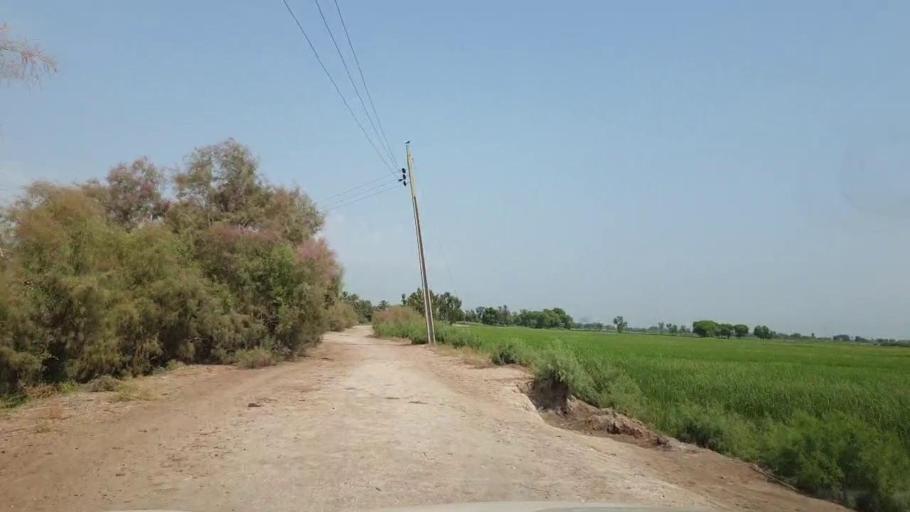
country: PK
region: Sindh
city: Ratodero
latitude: 27.8423
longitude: 68.2468
